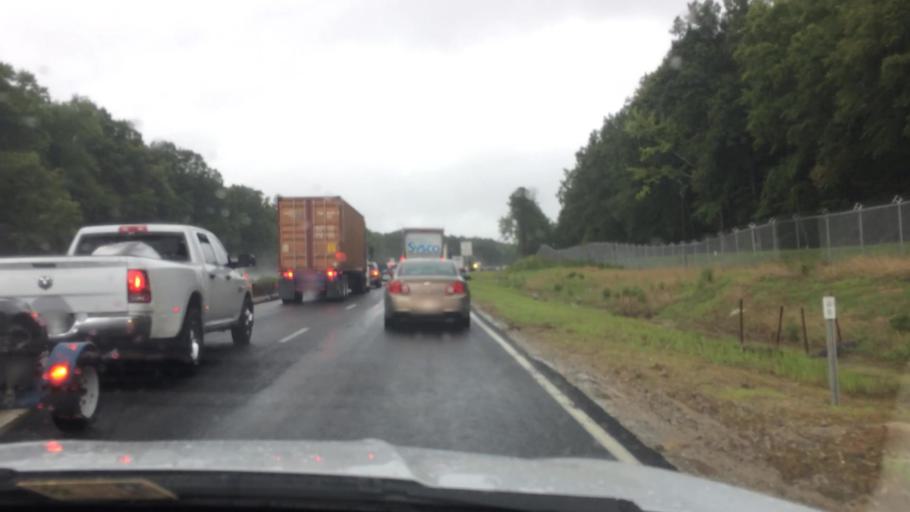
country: US
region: Virginia
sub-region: York County
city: Yorktown
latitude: 37.2168
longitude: -76.5986
